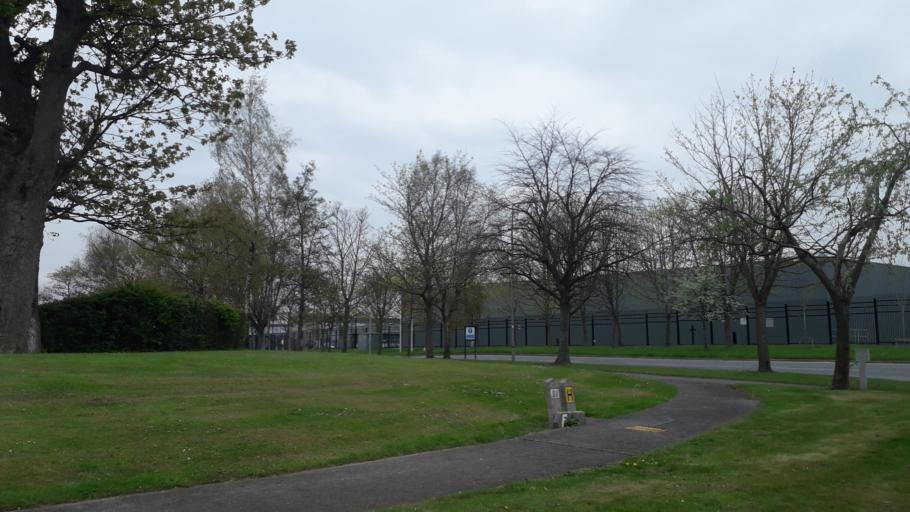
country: IE
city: Bonnybrook
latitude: 53.4023
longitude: -6.2180
